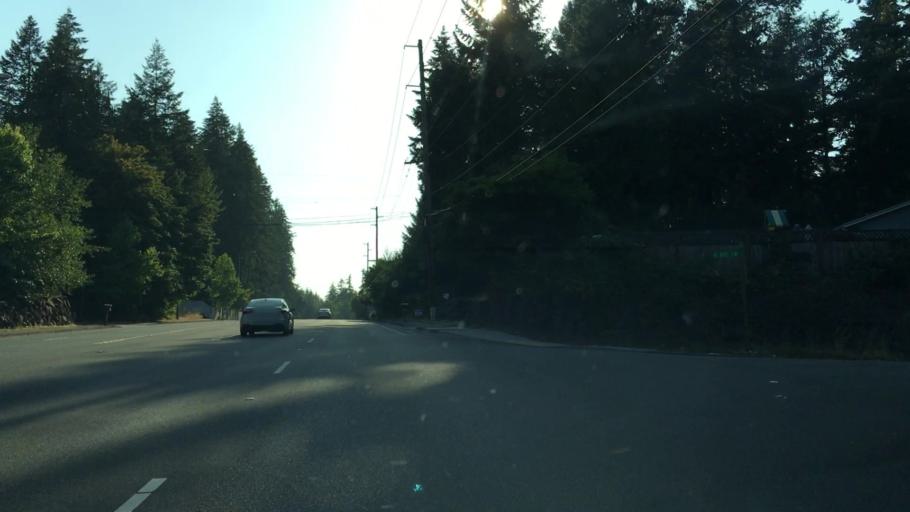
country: US
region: Washington
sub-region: Pierce County
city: Fife Heights
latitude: 47.2825
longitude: -122.3397
